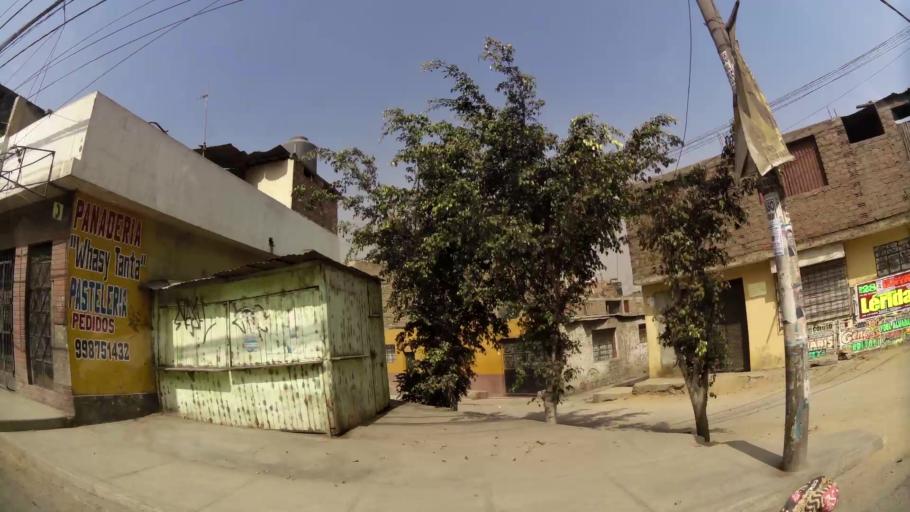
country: PE
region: Lima
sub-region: Lima
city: Asentamiento Humano Nicolas de Pierola
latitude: -11.9270
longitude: -76.6875
